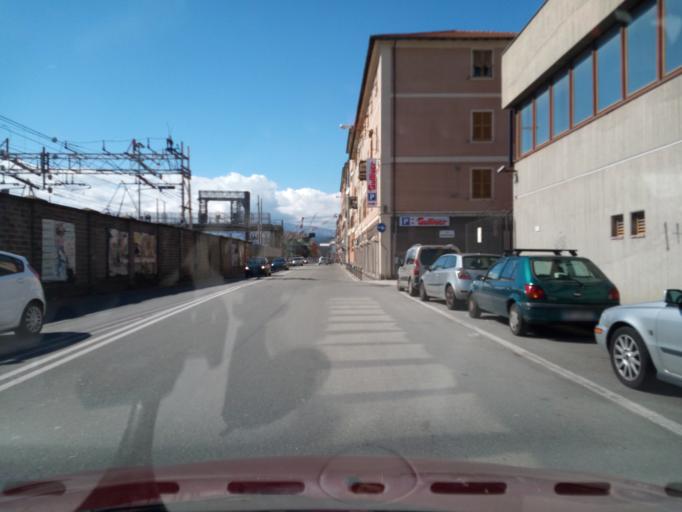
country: IT
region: Liguria
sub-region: Provincia di Genova
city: San Teodoro
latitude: 44.4219
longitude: 8.8511
